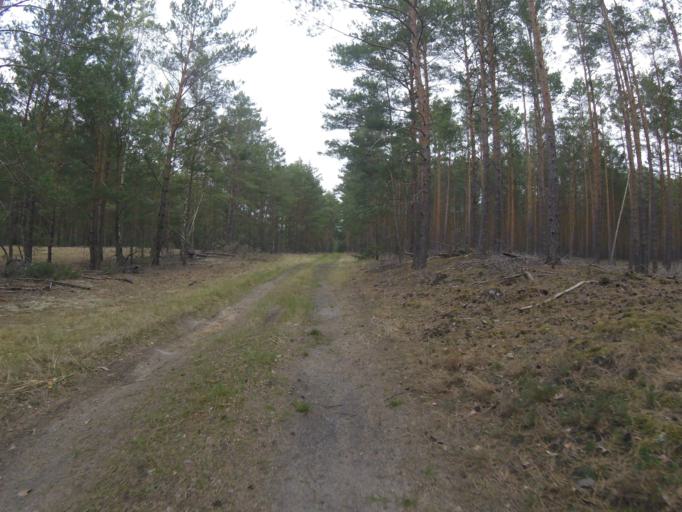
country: DE
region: Brandenburg
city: Gross Koris
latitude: 52.1471
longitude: 13.6565
